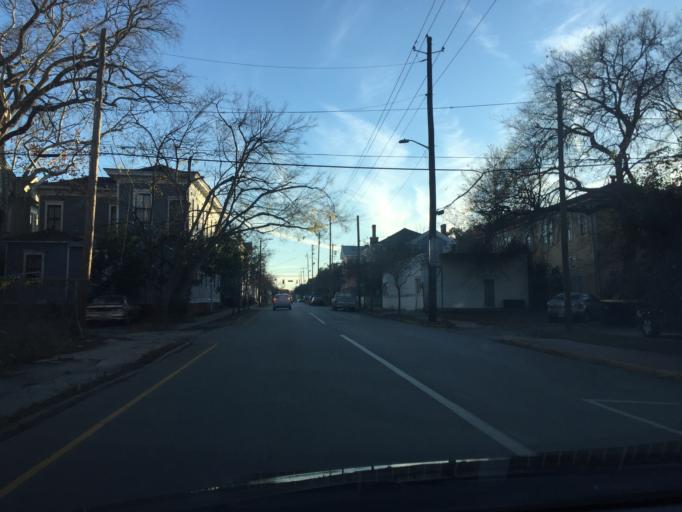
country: US
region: Georgia
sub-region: Chatham County
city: Savannah
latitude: 32.0632
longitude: -81.0920
